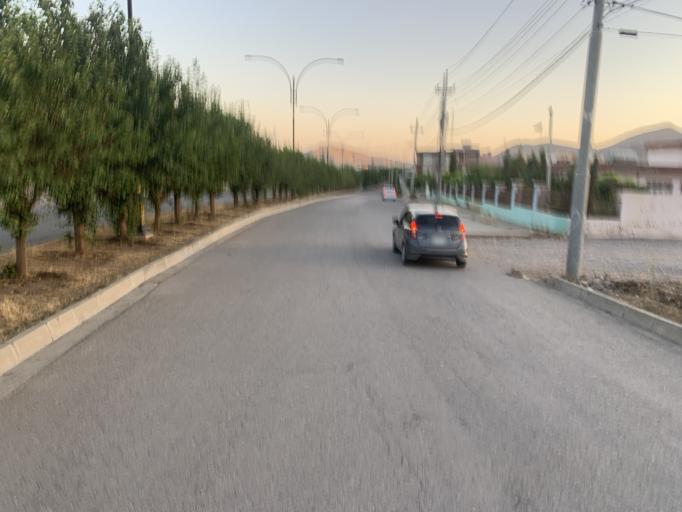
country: IQ
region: As Sulaymaniyah
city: Raniye
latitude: 36.2436
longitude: 44.8770
